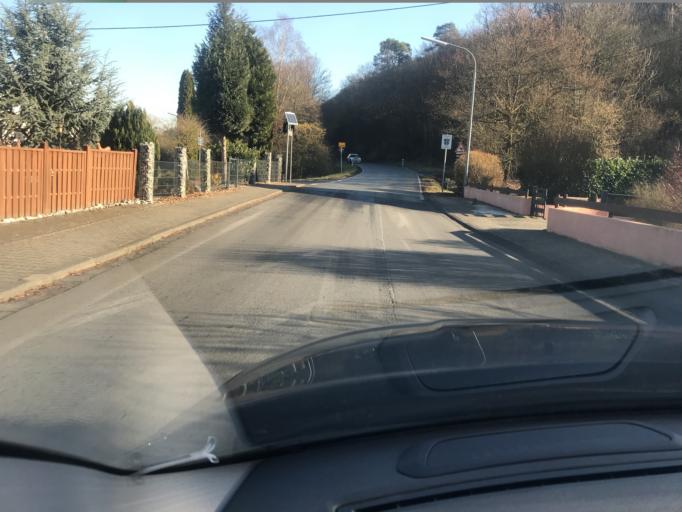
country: DE
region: Rheinland-Pfalz
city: Niedererbach
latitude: 50.4227
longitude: 7.9823
